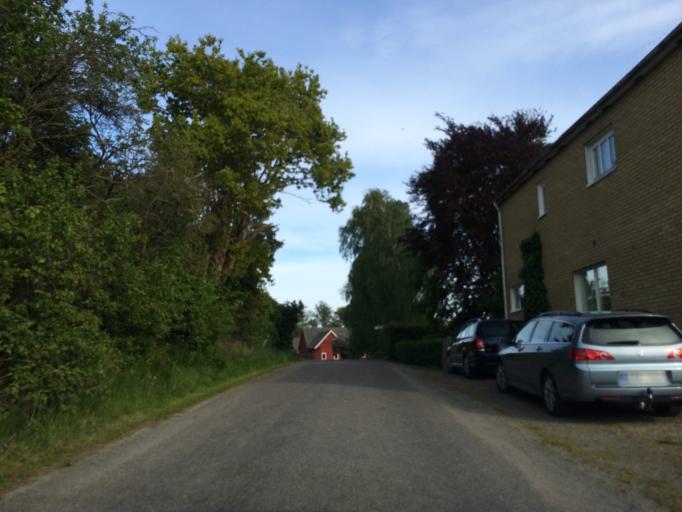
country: SE
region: Blekinge
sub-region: Karlshamns Kommun
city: Morrum
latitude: 56.1792
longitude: 14.7822
